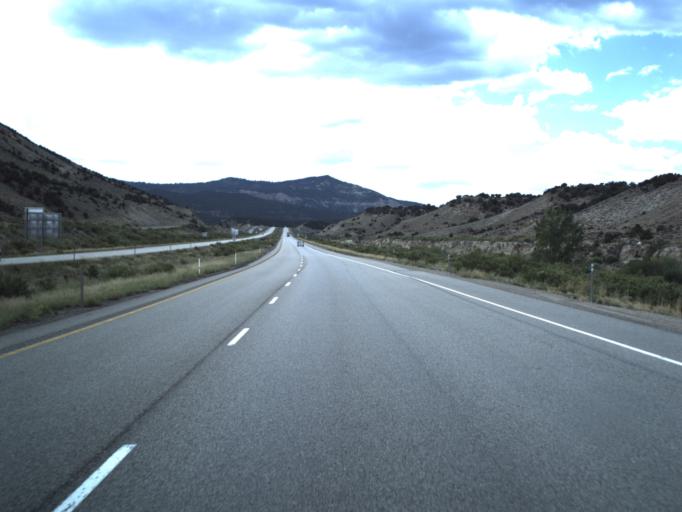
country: US
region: Utah
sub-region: Emery County
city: Ferron
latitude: 38.7649
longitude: -111.3563
